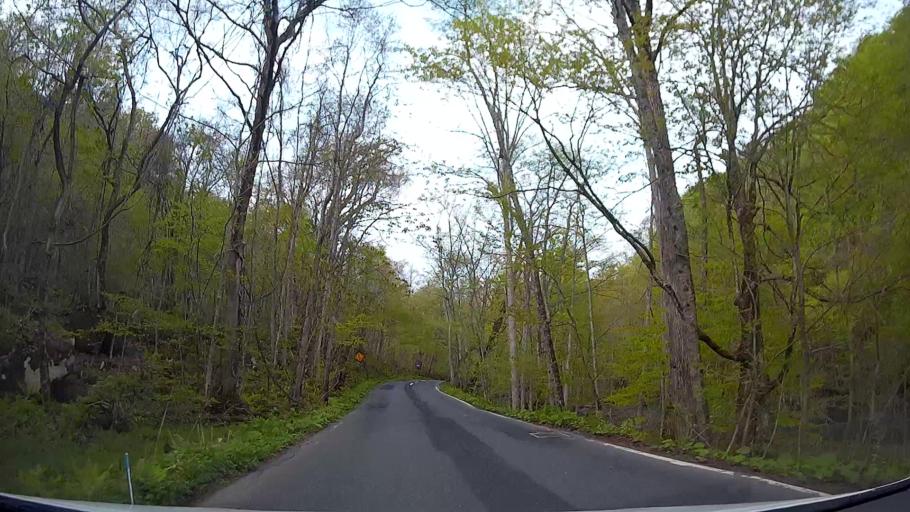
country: JP
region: Aomori
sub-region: Aomori Shi
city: Furudate
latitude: 40.5220
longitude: 140.9728
